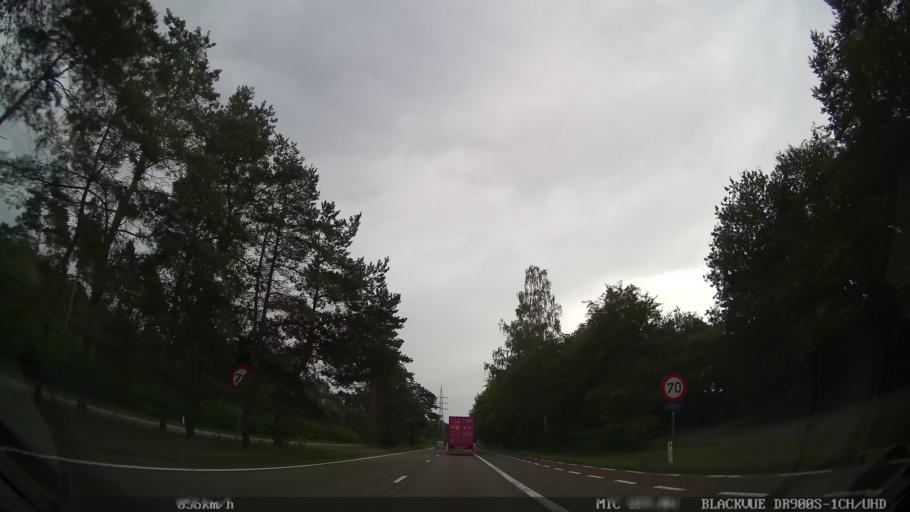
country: BE
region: Flanders
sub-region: Provincie Limburg
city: Genk
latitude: 50.9519
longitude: 5.5229
